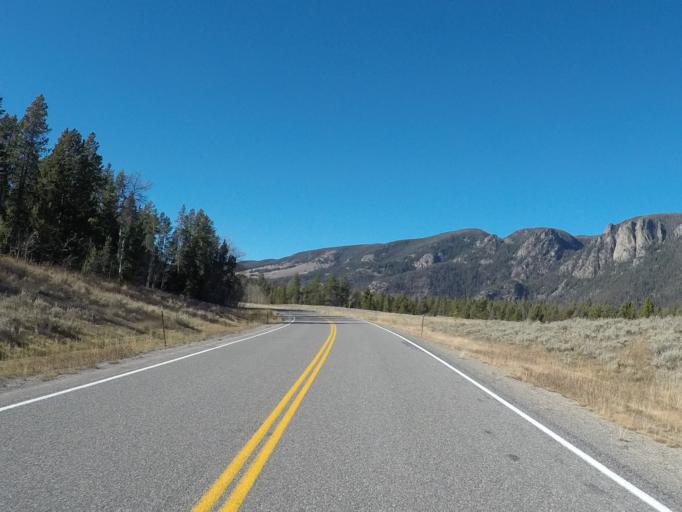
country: US
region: Montana
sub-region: Carbon County
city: Red Lodge
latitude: 44.8568
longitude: -109.5125
